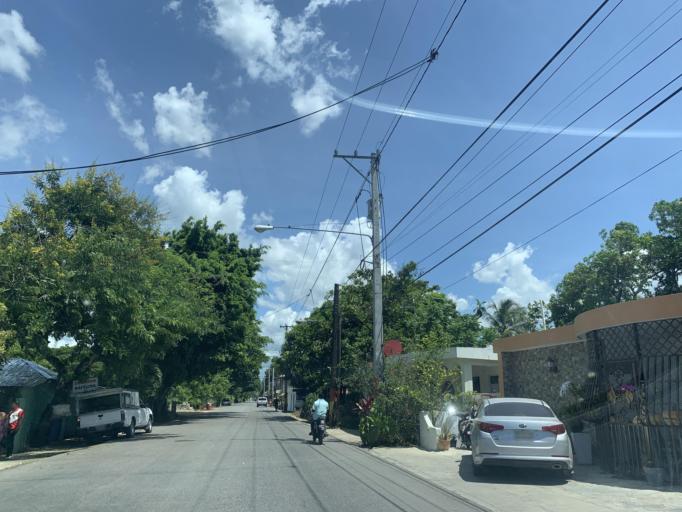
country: DO
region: Puerto Plata
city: Cabarete
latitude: 19.7004
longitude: -70.3828
